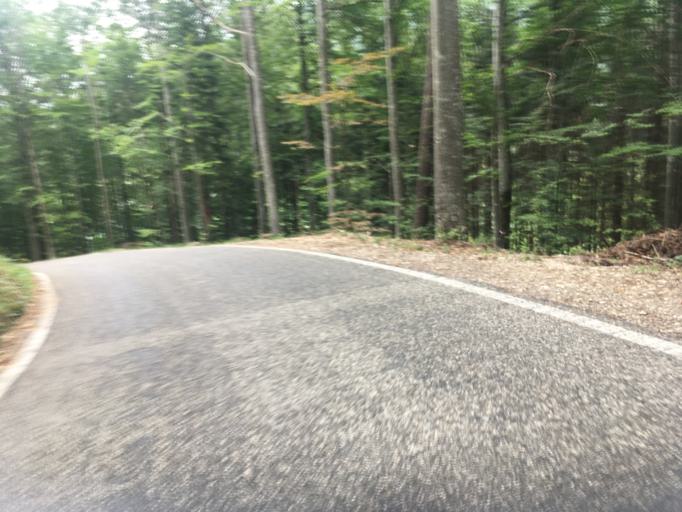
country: CH
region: Solothurn
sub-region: Bezirk Thal
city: Welschenrohr
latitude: 47.2611
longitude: 7.4830
